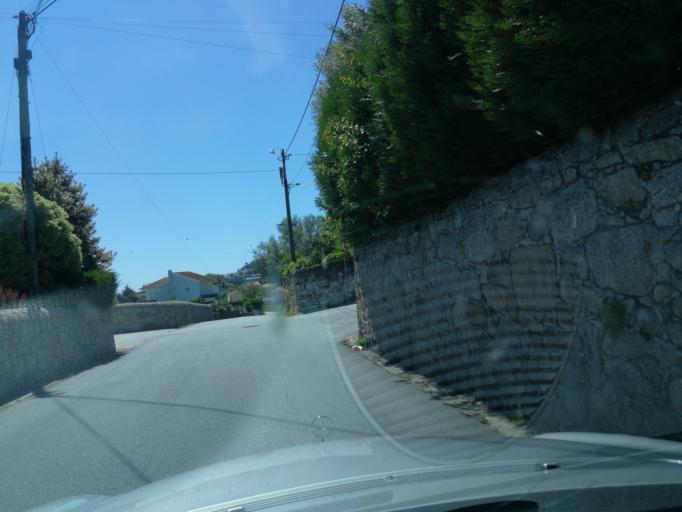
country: PT
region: Viana do Castelo
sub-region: Viana do Castelo
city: Meadela
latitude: 41.7230
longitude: -8.7932
